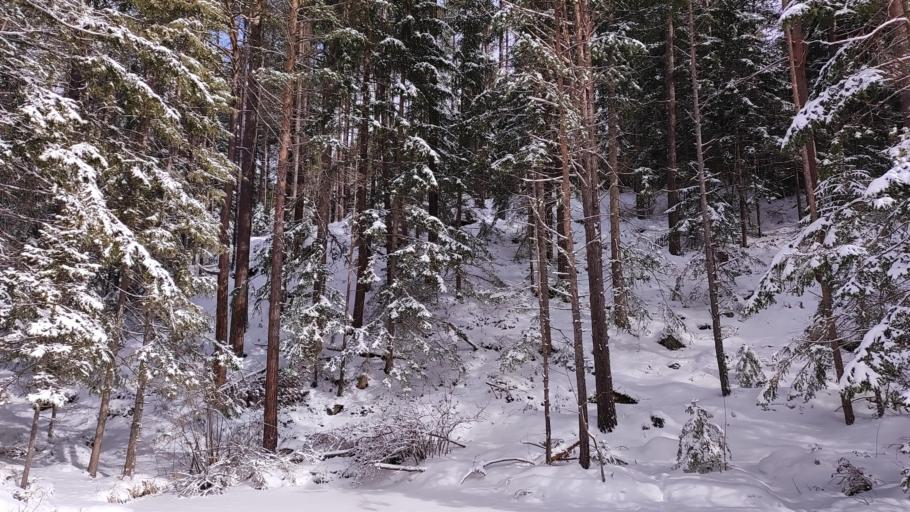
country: AT
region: Tyrol
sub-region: Politischer Bezirk Imst
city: Umhausen
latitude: 47.1032
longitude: 10.9338
